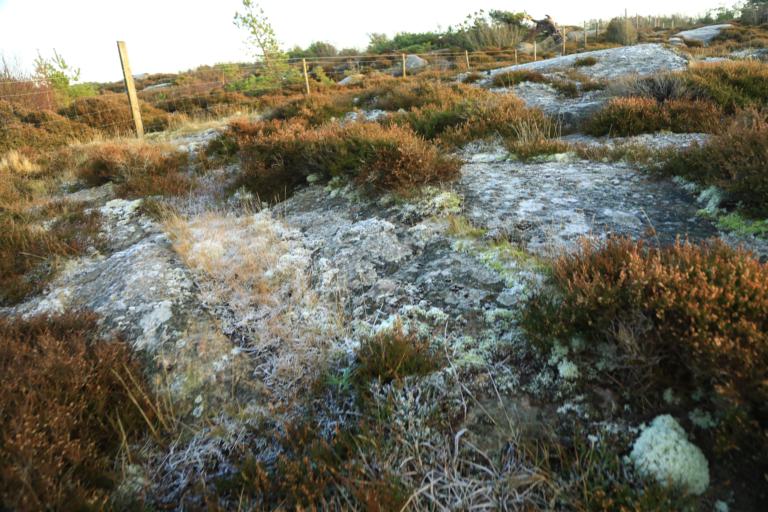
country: SE
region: Halland
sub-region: Kungsbacka Kommun
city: Frillesas
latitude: 57.1945
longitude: 12.1637
